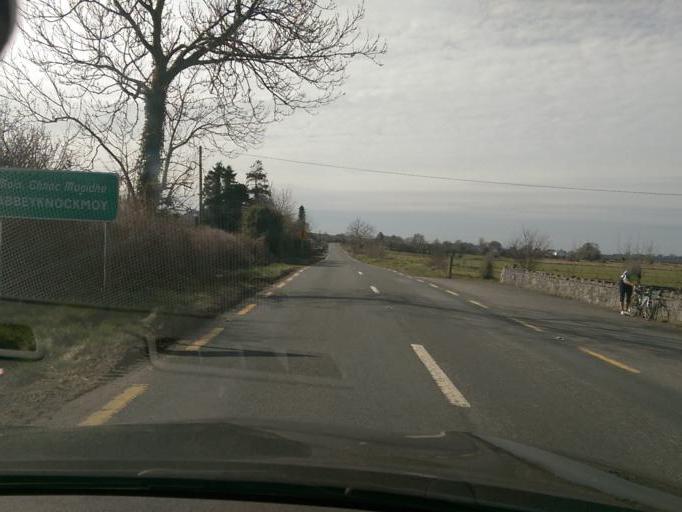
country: IE
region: Connaught
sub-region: County Galway
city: Tuam
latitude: 53.4383
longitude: -8.7362
